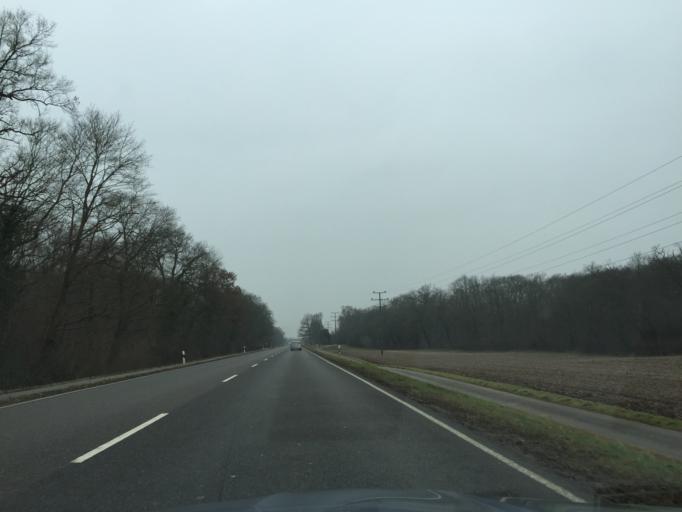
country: DE
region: Baden-Wuerttemberg
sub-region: Karlsruhe Region
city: Ketsch
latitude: 49.3720
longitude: 8.5570
